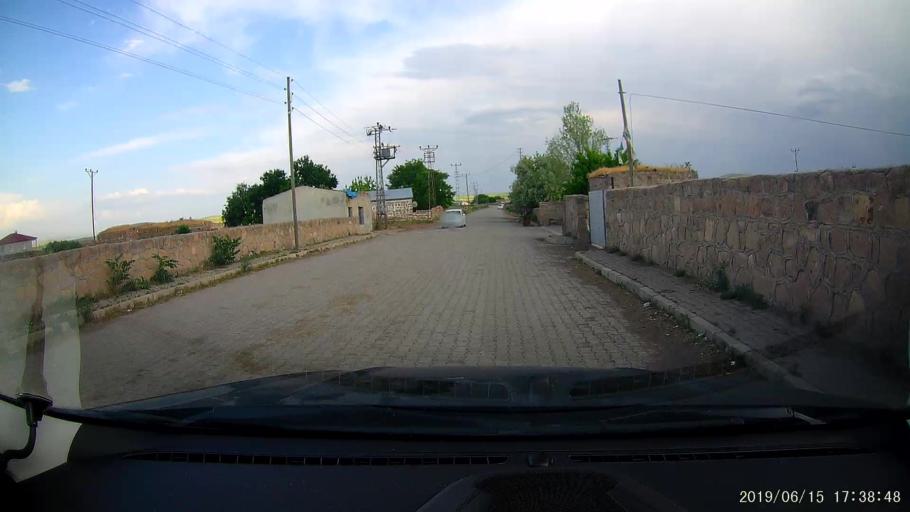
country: TR
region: Kars
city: Basgedikler
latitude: 40.5191
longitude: 43.5682
